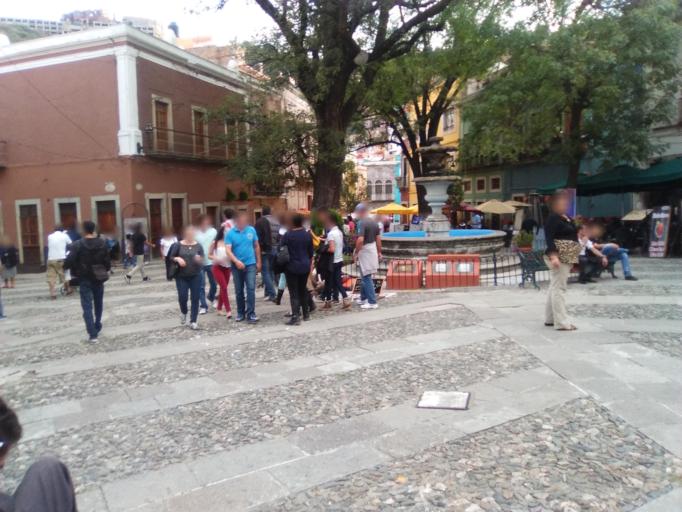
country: MX
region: Guanajuato
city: Guanajuato
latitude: 21.0177
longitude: -101.2561
